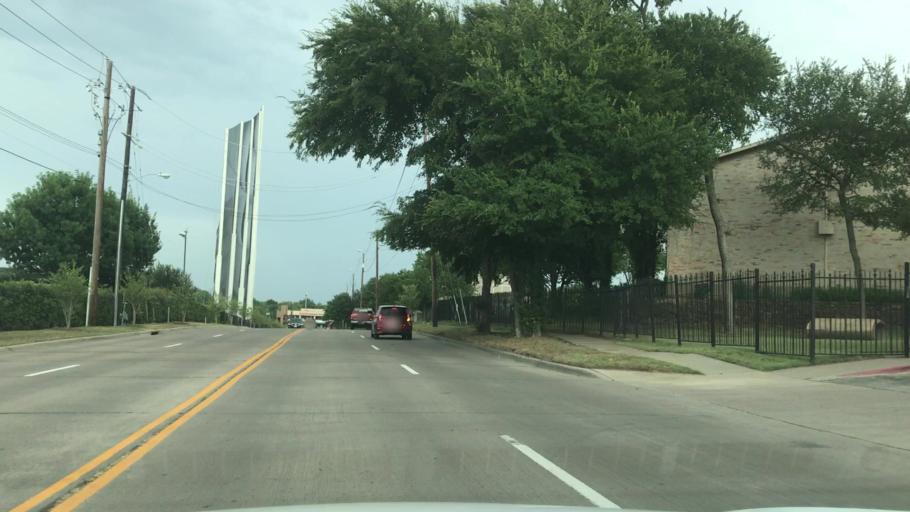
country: US
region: Texas
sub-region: Dallas County
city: University Park
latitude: 32.8689
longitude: -96.7474
